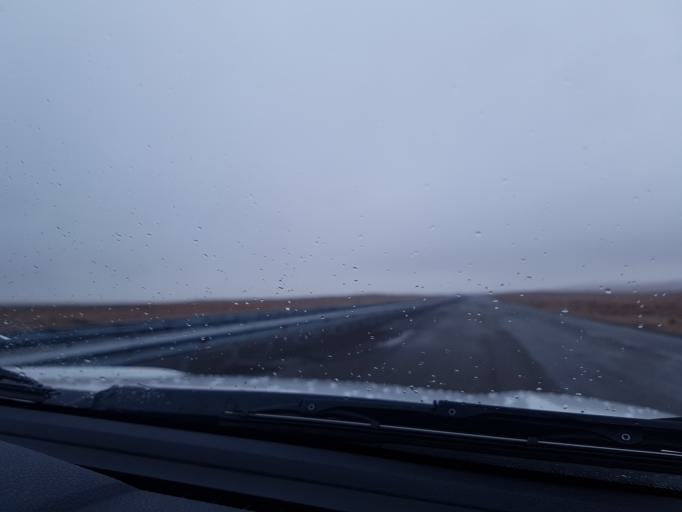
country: TM
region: Balkan
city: Balkanabat
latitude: 39.9786
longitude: 53.7809
